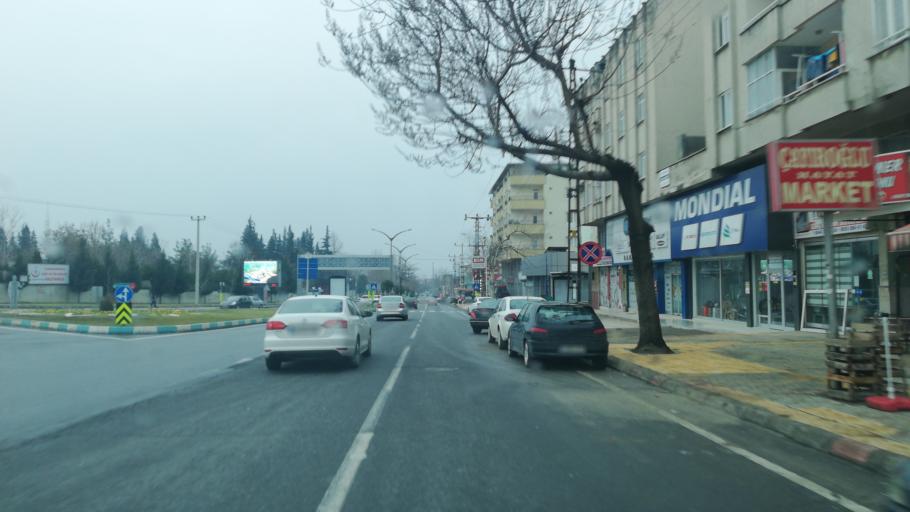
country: TR
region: Kahramanmaras
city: Kahramanmaras
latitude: 37.5667
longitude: 36.9492
